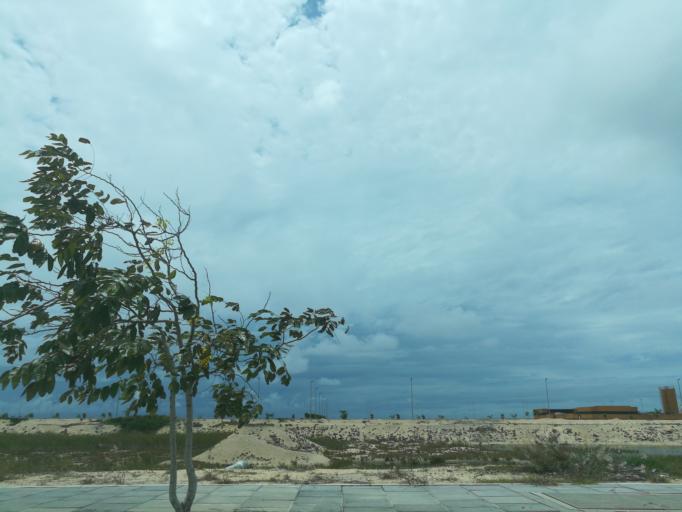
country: NG
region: Lagos
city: Lagos
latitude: 6.4072
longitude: 3.4130
